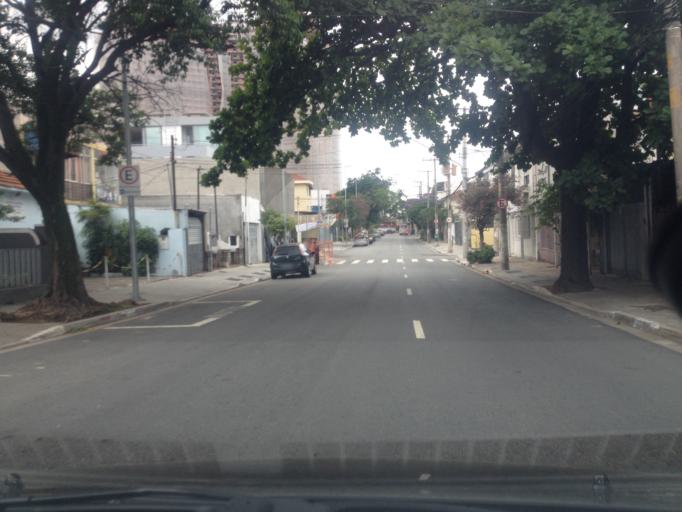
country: BR
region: Sao Paulo
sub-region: Sao Paulo
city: Sao Paulo
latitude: -23.5656
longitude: -46.6992
